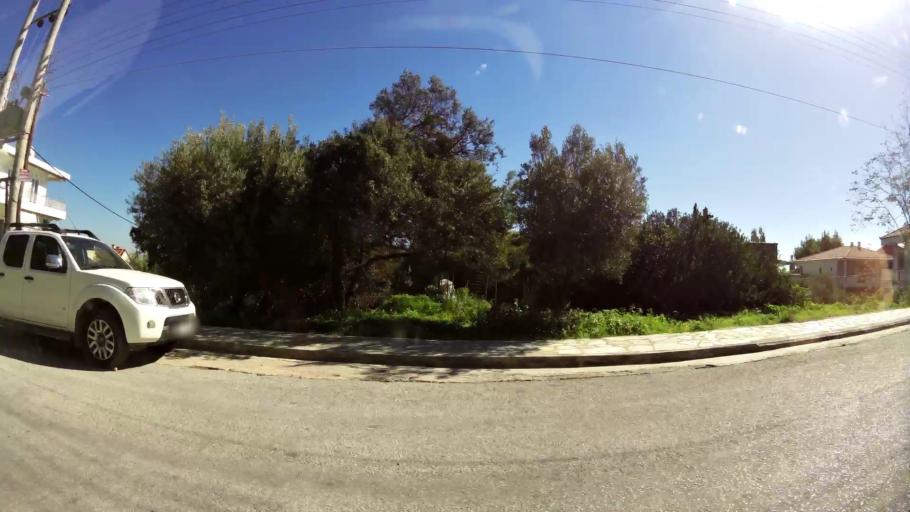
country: GR
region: Attica
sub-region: Nomarchia Anatolikis Attikis
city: Leondarion
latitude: 37.9846
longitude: 23.8601
